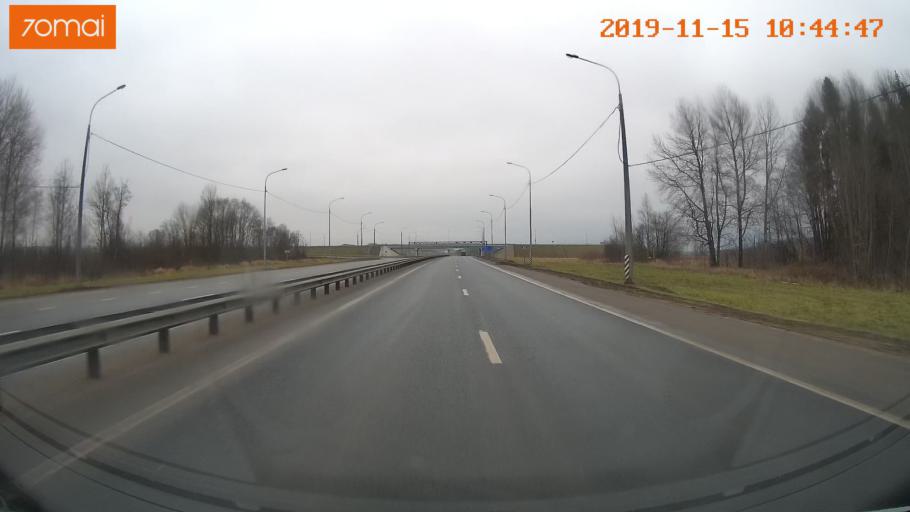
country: RU
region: Vologda
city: Sheksna
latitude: 59.2116
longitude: 38.5680
